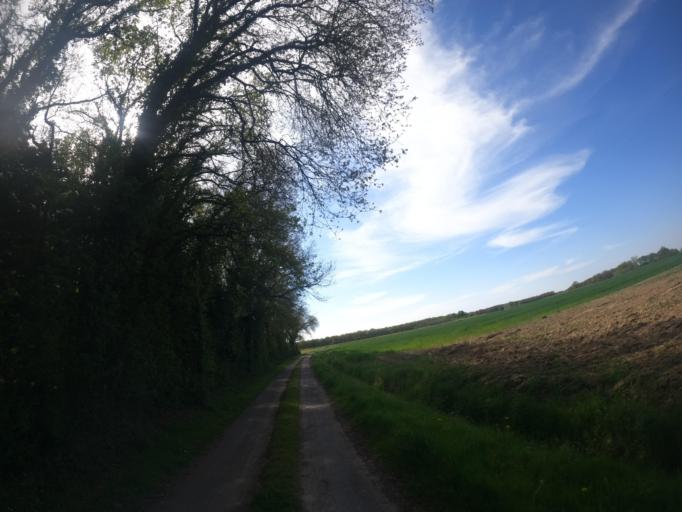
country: FR
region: Poitou-Charentes
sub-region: Departement des Deux-Sevres
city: Saint-Varent
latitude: 46.9257
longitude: -0.2297
